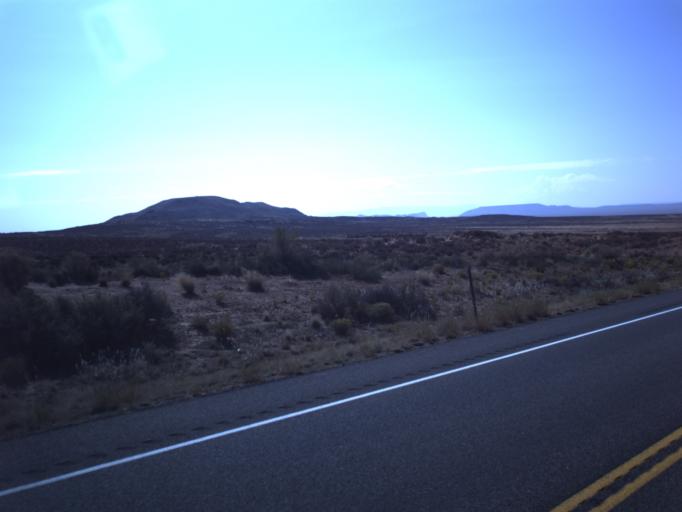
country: US
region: Utah
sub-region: San Juan County
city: Blanding
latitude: 37.3503
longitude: -109.5188
